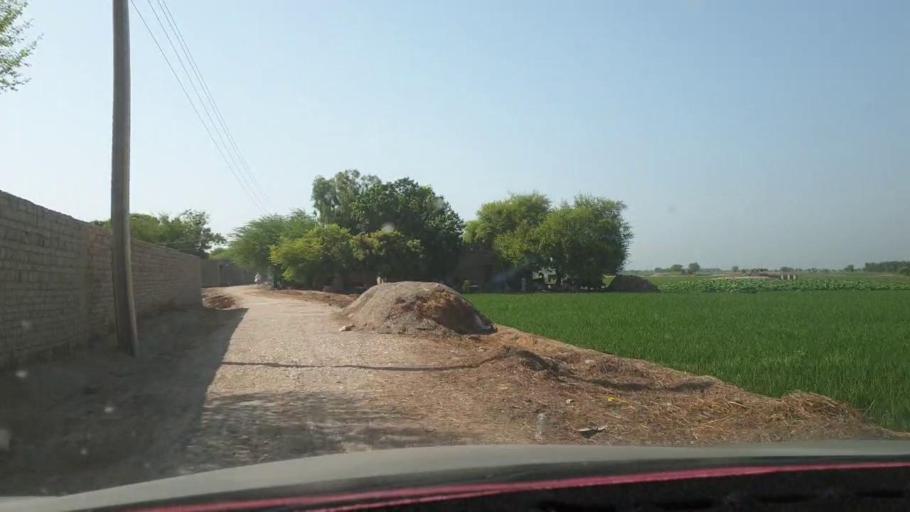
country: PK
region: Sindh
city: Nasirabad
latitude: 27.3828
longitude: 67.8793
